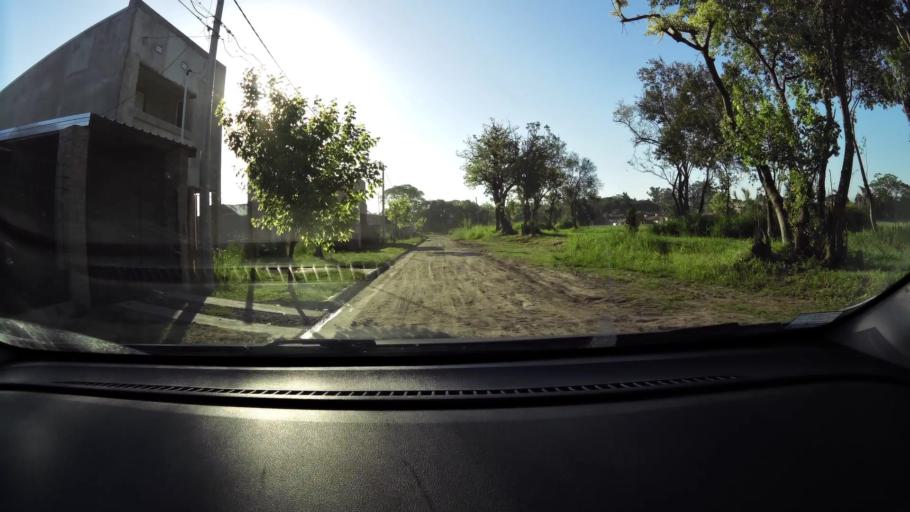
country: AR
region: Santa Fe
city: Santa Fe de la Vera Cruz
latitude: -31.5884
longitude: -60.6886
